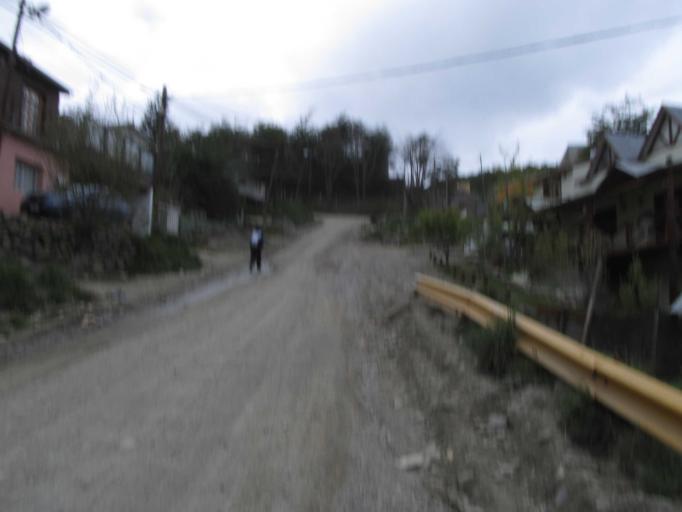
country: AR
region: Tierra del Fuego
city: Ushuaia
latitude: -54.7977
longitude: -68.2822
